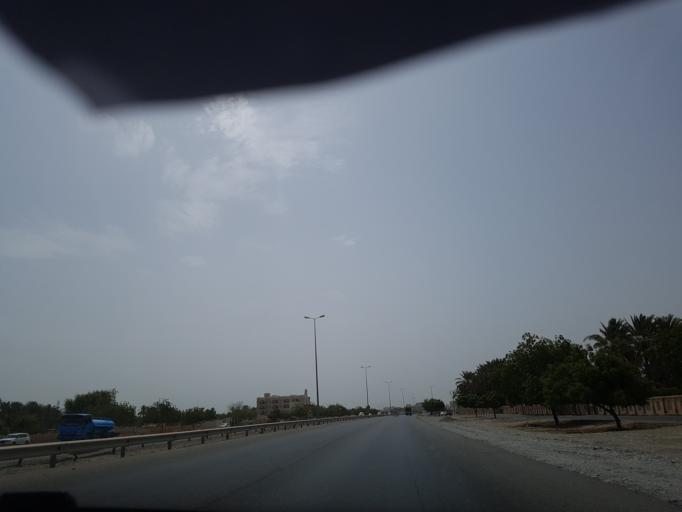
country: OM
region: Al Batinah
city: As Suwayq
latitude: 23.7507
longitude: 57.6132
